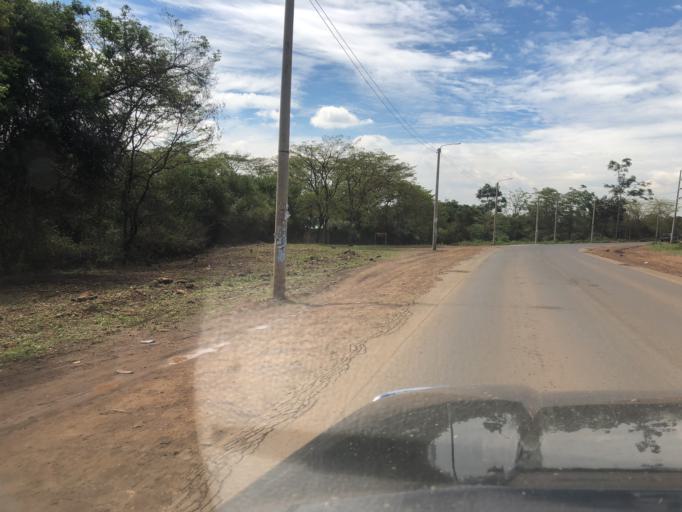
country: KE
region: Nairobi Area
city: Nairobi
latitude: -1.3668
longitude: 36.7673
